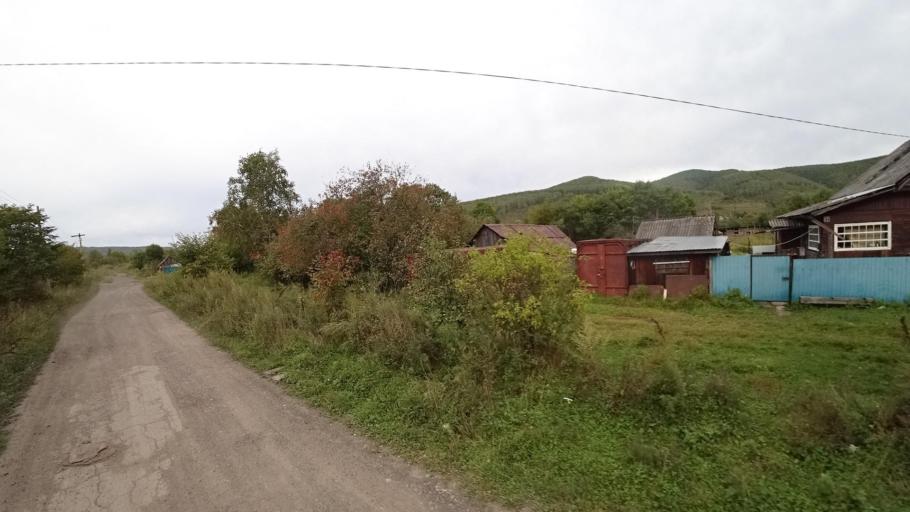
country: RU
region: Jewish Autonomous Oblast
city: Khingansk
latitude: 49.0401
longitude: 131.0497
